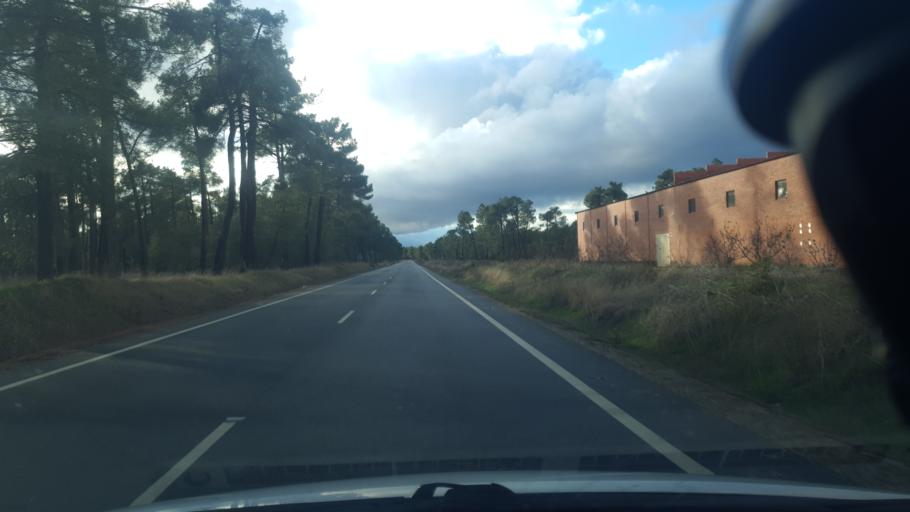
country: ES
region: Castille and Leon
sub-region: Provincia de Segovia
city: Nava de la Asuncion
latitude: 41.1558
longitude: -4.5145
